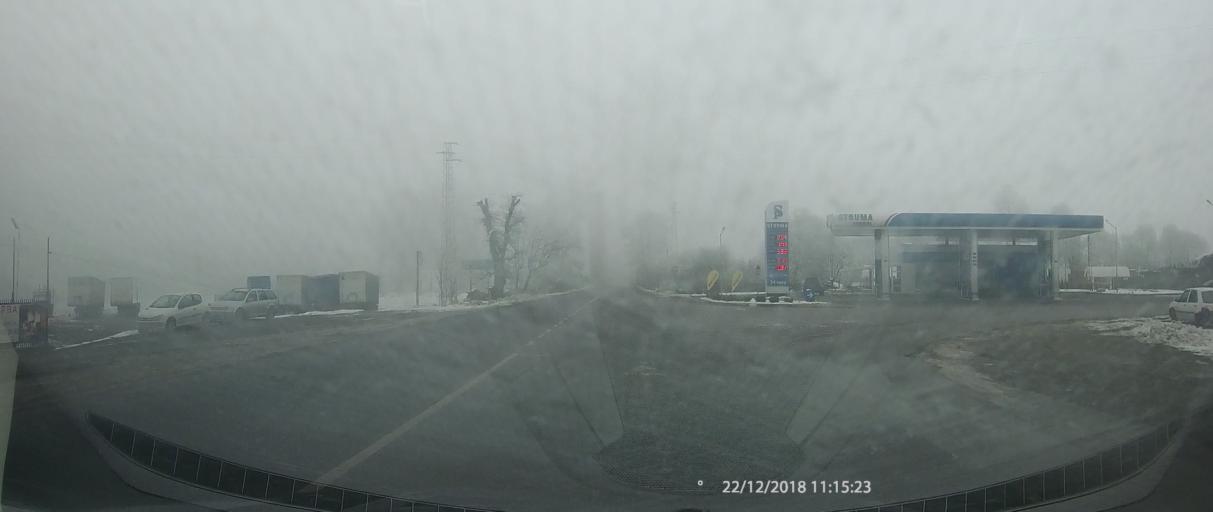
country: BG
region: Kyustendil
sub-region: Obshtina Kyustendil
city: Kyustendil
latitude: 42.2815
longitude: 22.7222
